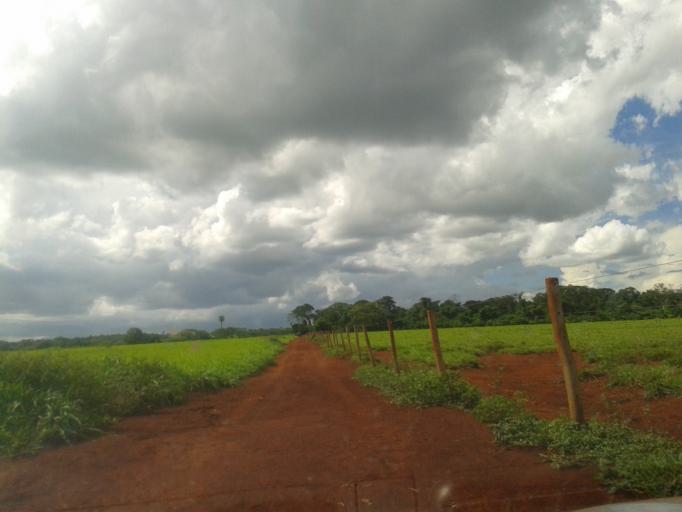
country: BR
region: Minas Gerais
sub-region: Capinopolis
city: Capinopolis
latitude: -18.7777
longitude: -49.8260
